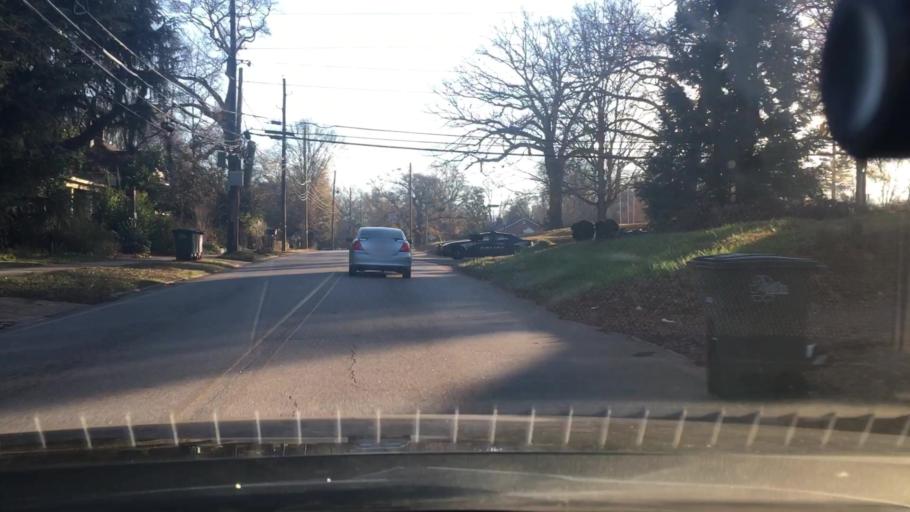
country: US
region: Georgia
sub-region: Spalding County
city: Griffin
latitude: 33.2459
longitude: -84.2778
